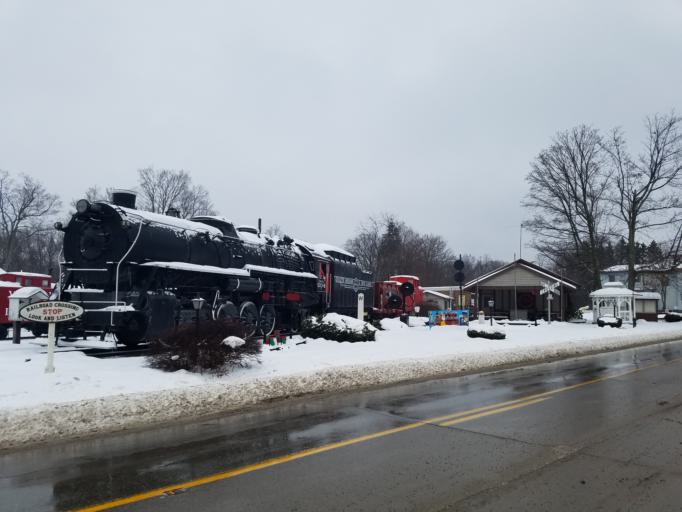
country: US
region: Pennsylvania
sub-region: Mercer County
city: Greenville
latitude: 41.4073
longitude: -80.3818
